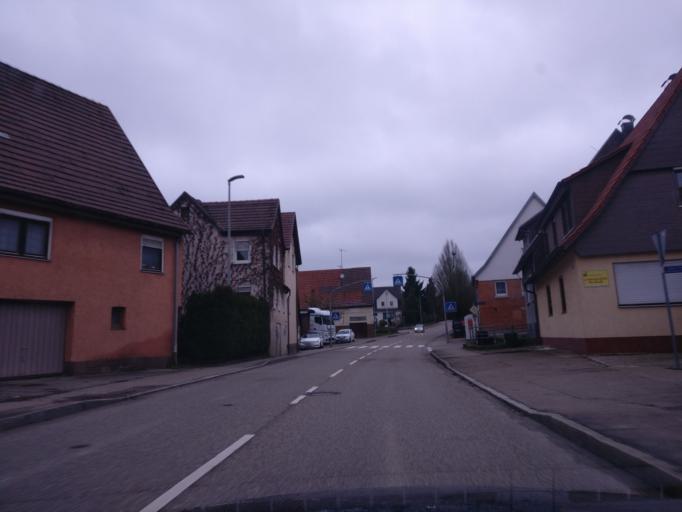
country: DE
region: Baden-Wuerttemberg
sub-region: Regierungsbezirk Stuttgart
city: Schorndorf
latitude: 48.8431
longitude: 9.5405
